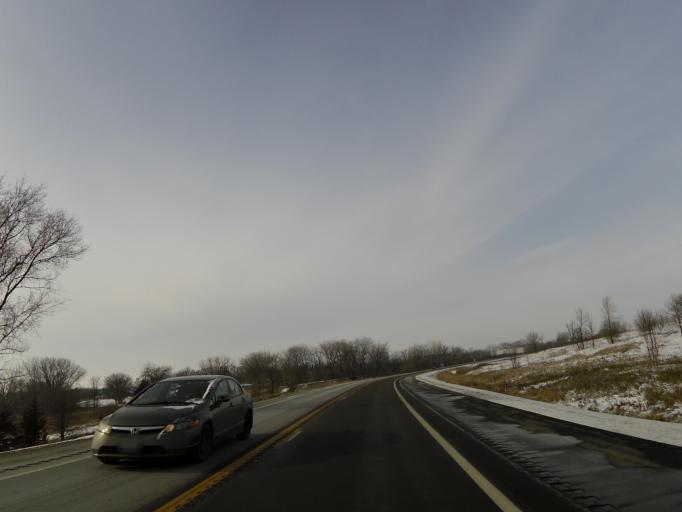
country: US
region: Minnesota
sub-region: McLeod County
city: Hutchinson
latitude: 44.8937
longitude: -94.4228
